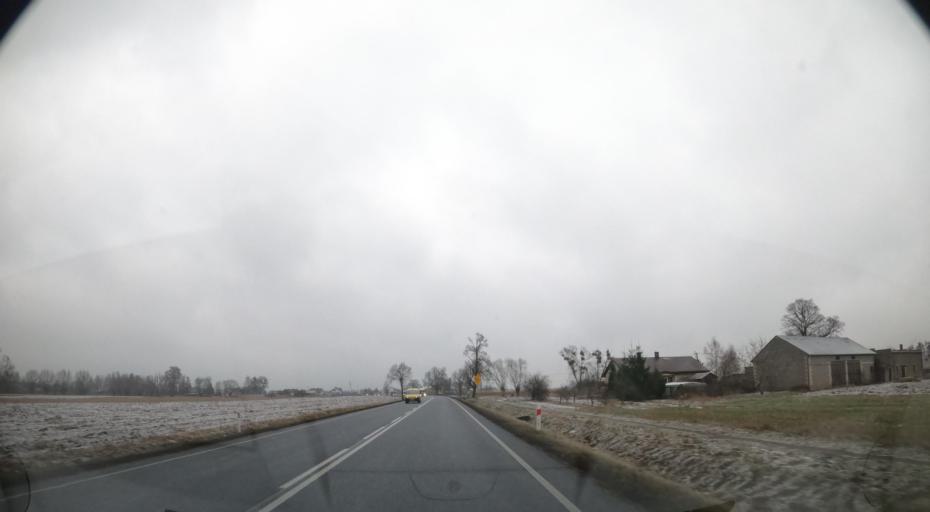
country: PL
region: Masovian Voivodeship
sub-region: Powiat sochaczewski
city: Mlodzieszyn
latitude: 52.2812
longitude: 20.1767
